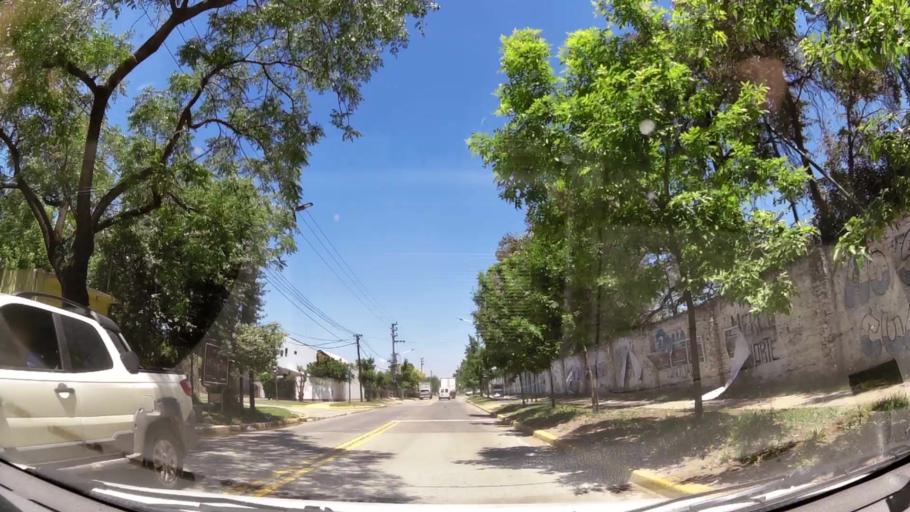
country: AR
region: Buenos Aires
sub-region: Partido de Merlo
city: Merlo
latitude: -34.6456
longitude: -58.7185
